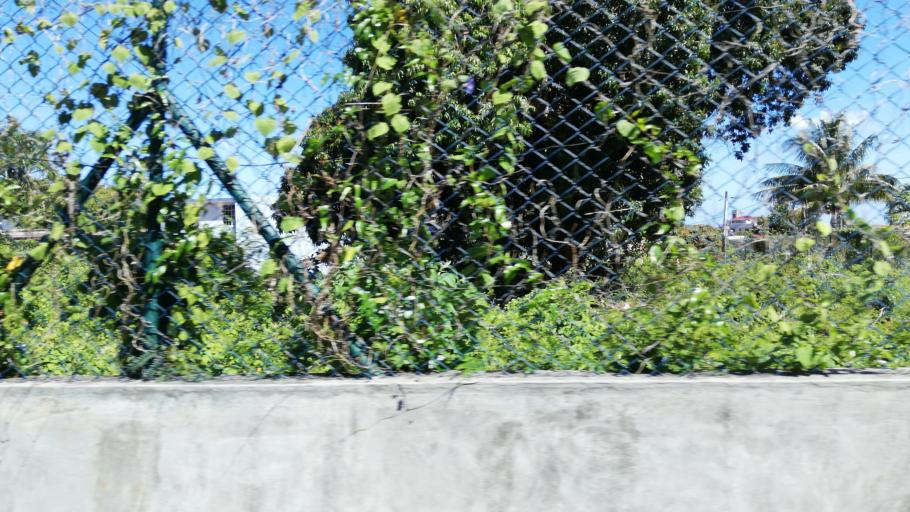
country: MU
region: Plaines Wilhems
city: Ebene
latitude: -20.2297
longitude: 57.4717
